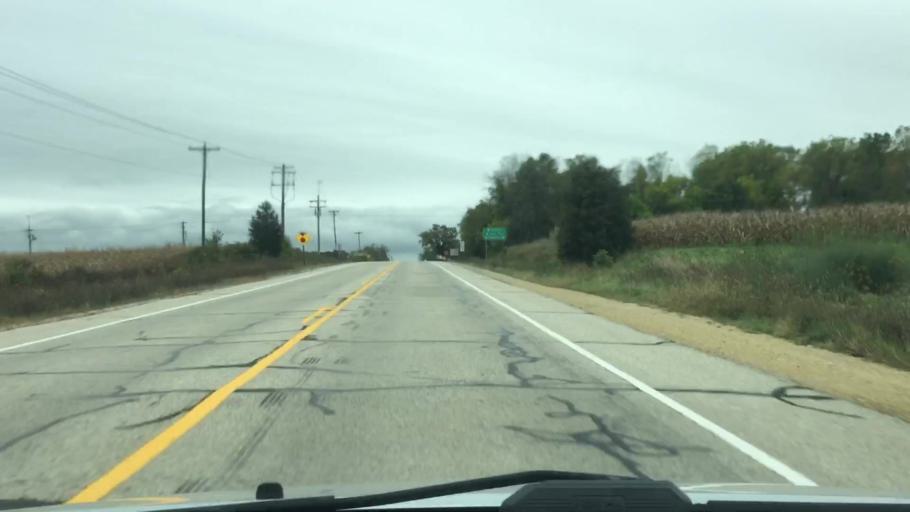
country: US
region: Wisconsin
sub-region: Jefferson County
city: Palmyra
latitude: 42.8020
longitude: -88.5628
